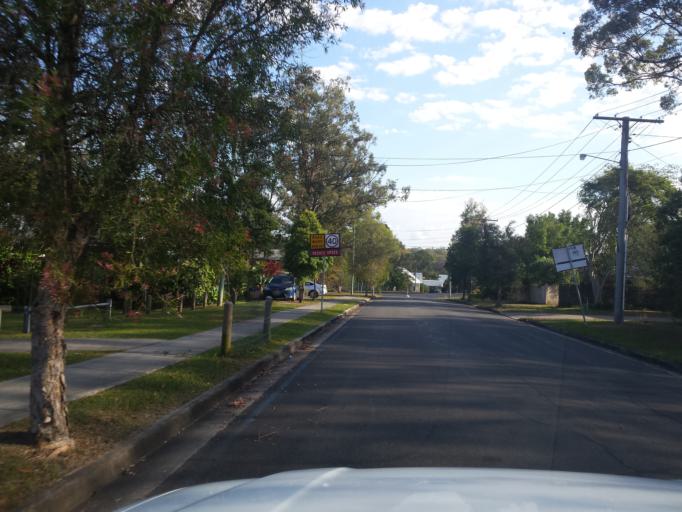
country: AU
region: Queensland
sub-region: Logan
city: Logan City
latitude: -27.6558
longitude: 153.1026
